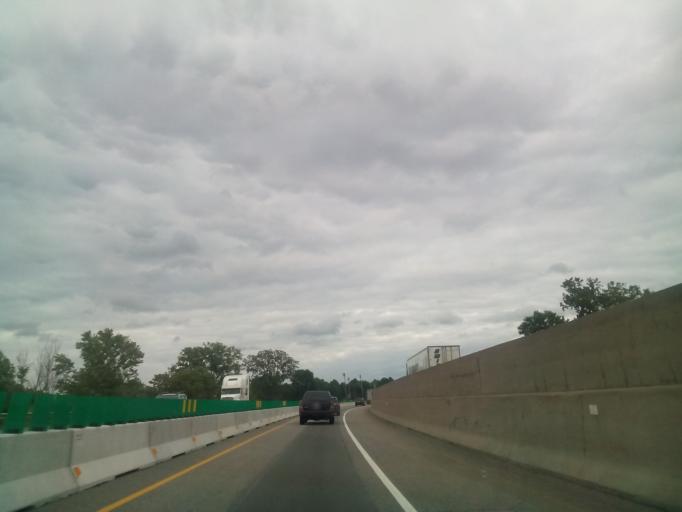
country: US
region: Ohio
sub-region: Lorain County
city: Elyria
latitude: 41.3864
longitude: -82.0765
